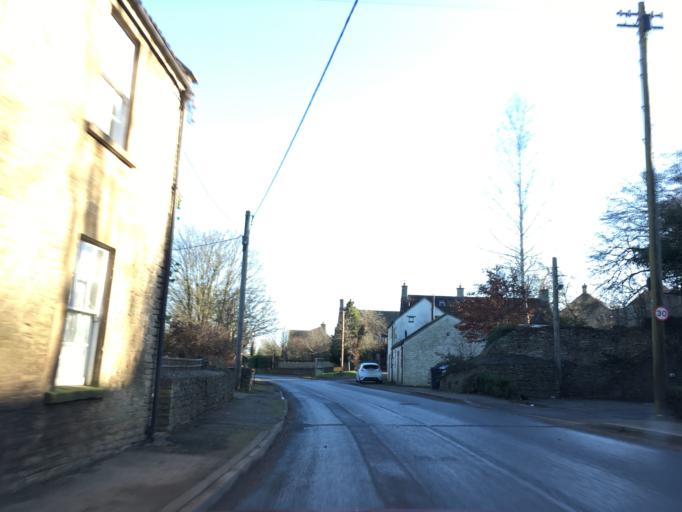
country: GB
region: England
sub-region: Wiltshire
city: Nettleton
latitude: 51.5143
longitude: -2.2665
